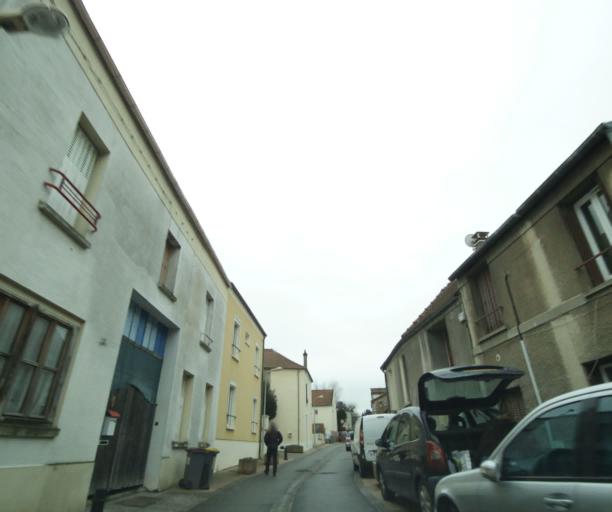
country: FR
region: Ile-de-France
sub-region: Departement de l'Essonne
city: Champlan
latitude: 48.7079
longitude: 2.2711
